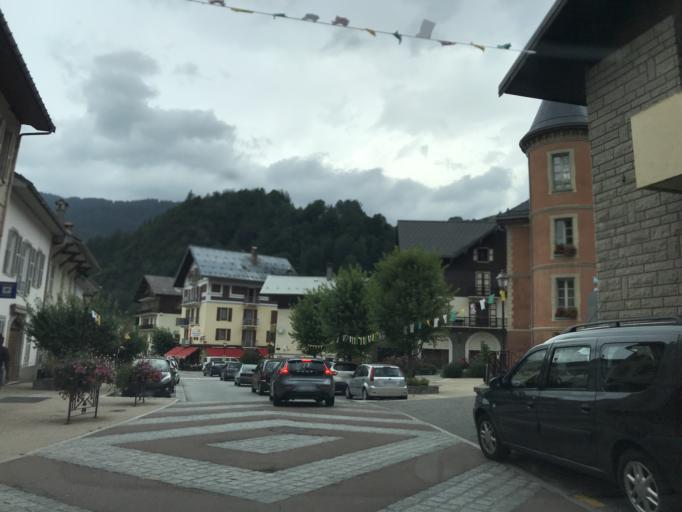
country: FR
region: Rhone-Alpes
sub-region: Departement de la Savoie
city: Beaufort
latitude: 45.7173
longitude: 6.5756
